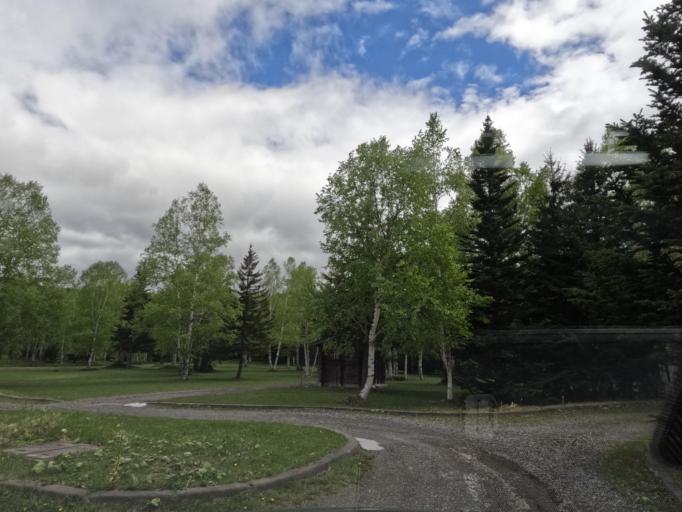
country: JP
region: Hokkaido
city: Kamikawa
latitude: 43.6447
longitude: 143.0224
